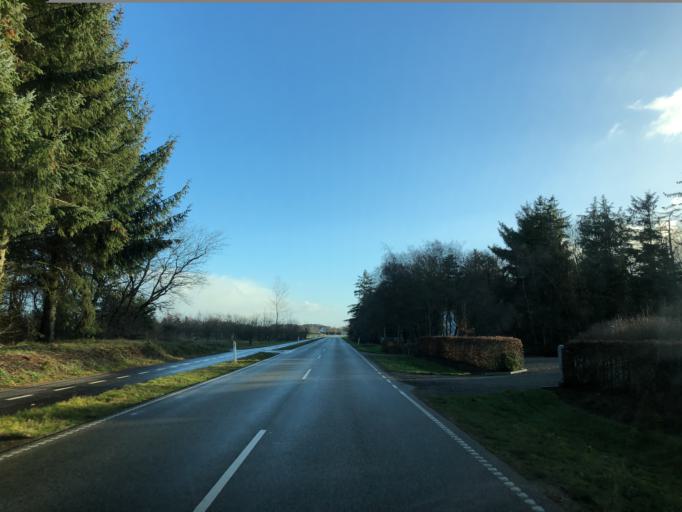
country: DK
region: Central Jutland
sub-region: Holstebro Kommune
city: Ulfborg
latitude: 56.1967
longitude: 8.2887
